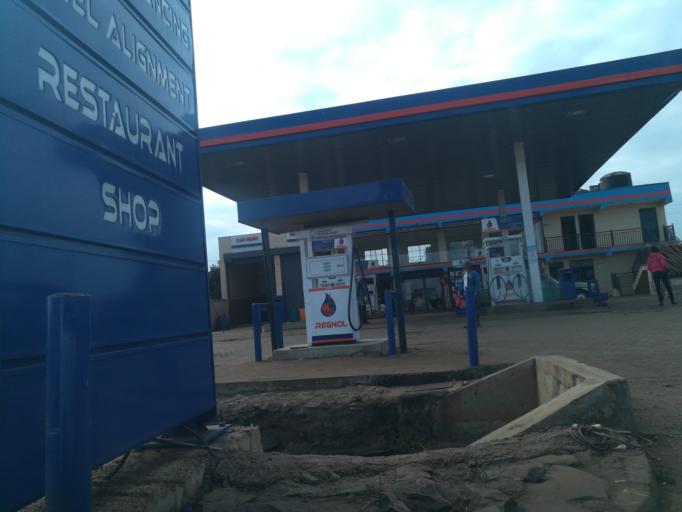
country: KE
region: Nairobi Area
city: Thika
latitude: -1.1298
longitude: 36.9845
